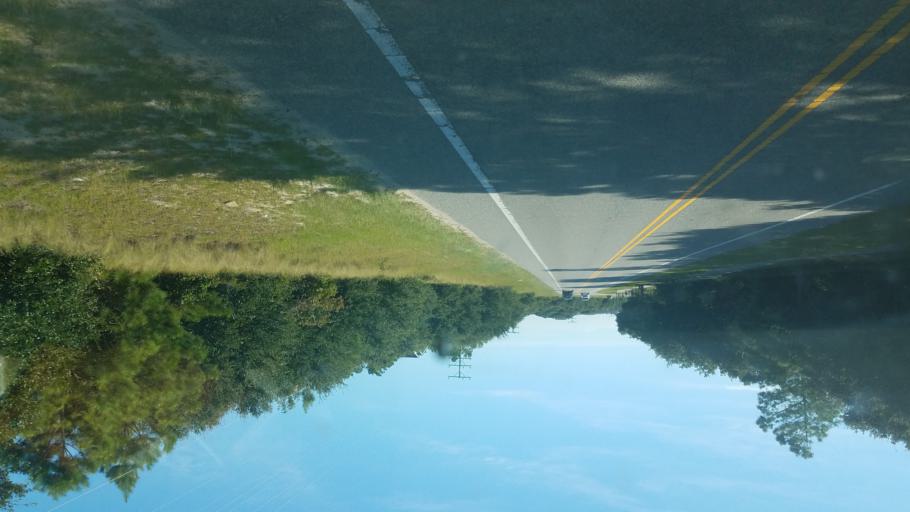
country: US
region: North Carolina
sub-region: Dare County
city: Southern Shores
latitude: 36.3183
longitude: -75.8146
